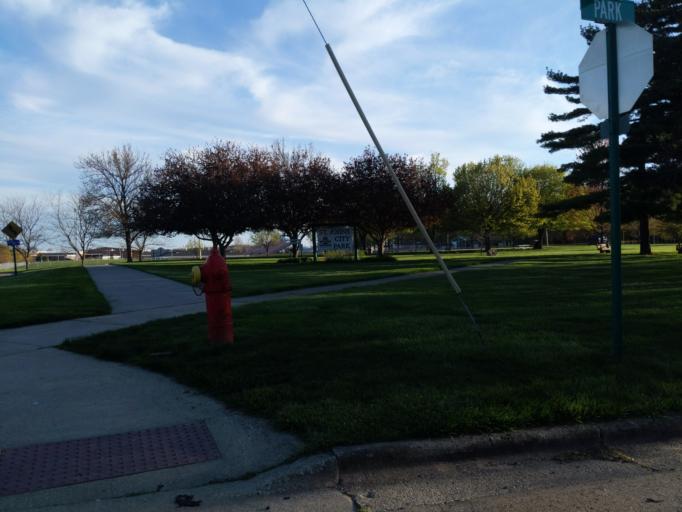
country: US
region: Michigan
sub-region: Clinton County
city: Saint Johns
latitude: 42.9972
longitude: -84.5668
